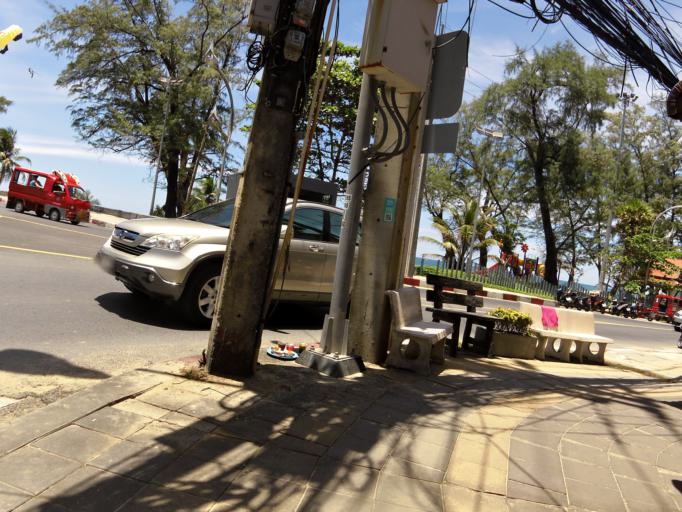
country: TH
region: Phuket
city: Ban Karon
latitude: 7.8494
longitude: 98.2932
